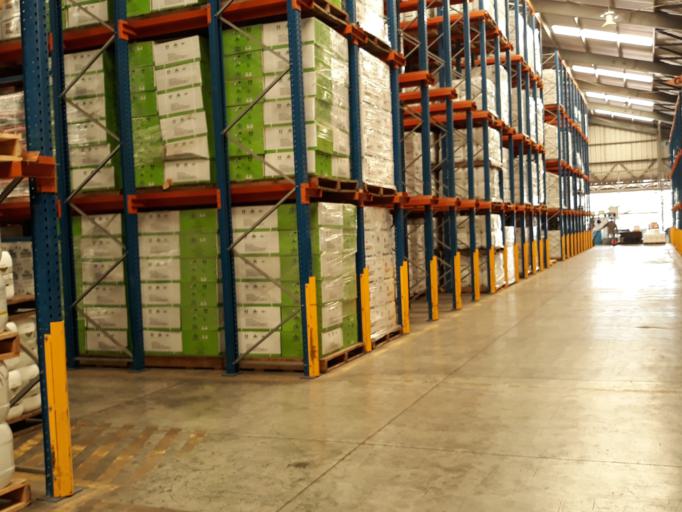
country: GT
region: Escuintla
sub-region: Municipio de Masagua
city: Masagua
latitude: 14.2144
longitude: -90.7572
